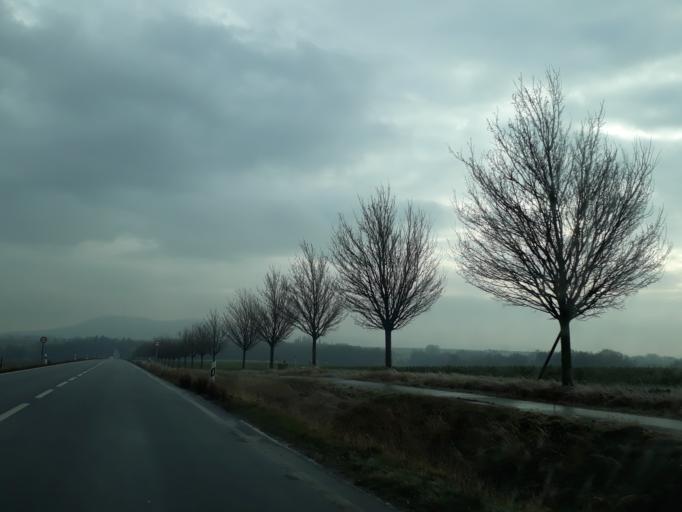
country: DE
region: Saxony
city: Lobau
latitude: 51.1241
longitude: 14.6292
